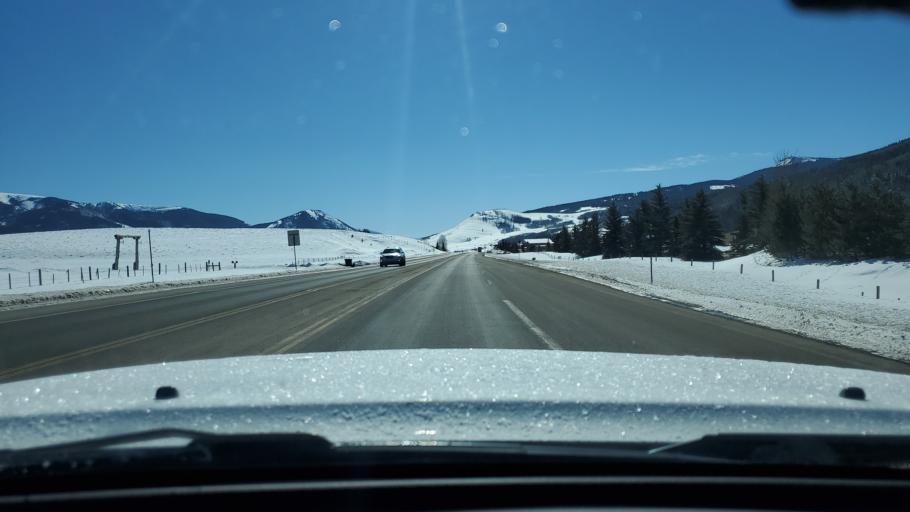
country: US
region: Colorado
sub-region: Gunnison County
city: Crested Butte
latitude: 38.8456
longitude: -106.9451
